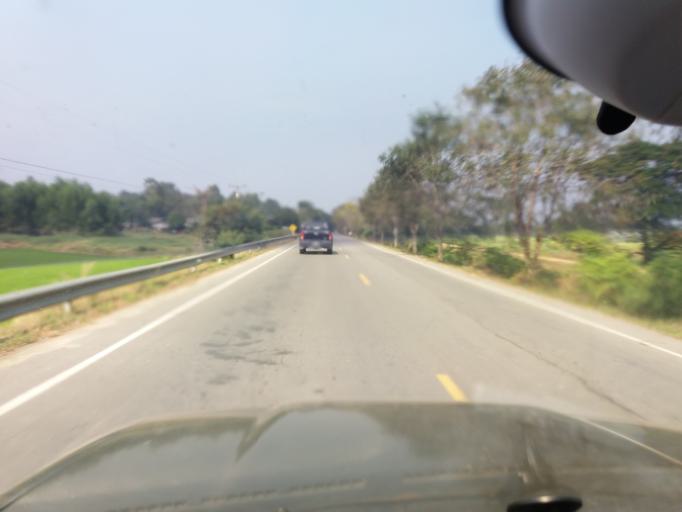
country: TH
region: Sing Buri
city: Bang Racham
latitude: 14.8817
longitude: 100.2772
